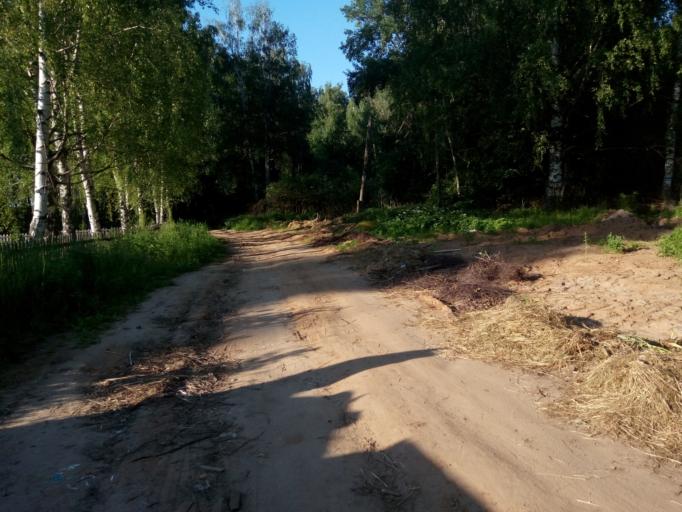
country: RU
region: Nizjnij Novgorod
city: Voskresenskoye
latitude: 56.7837
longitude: 45.5220
